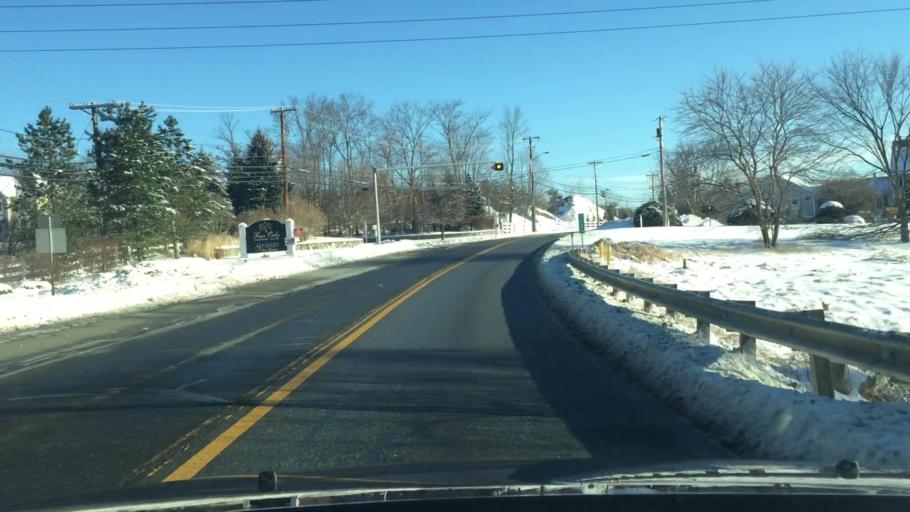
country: US
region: Massachusetts
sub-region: Middlesex County
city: Dracut
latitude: 42.6795
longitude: -71.2931
